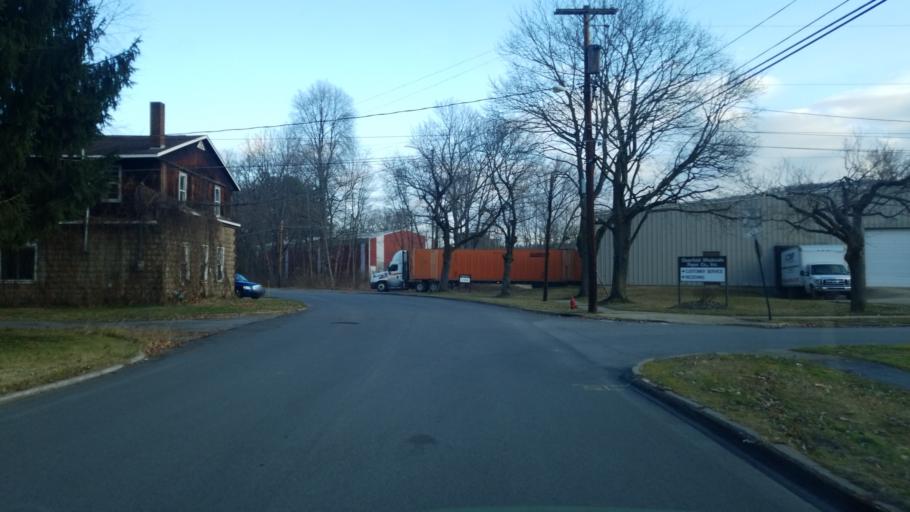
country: US
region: Pennsylvania
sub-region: Clearfield County
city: Clearfield
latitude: 41.0113
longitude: -78.4429
